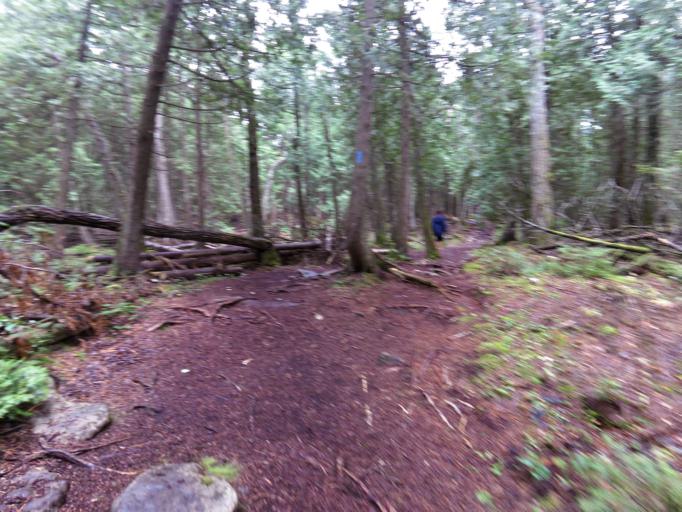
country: CA
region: Ontario
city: Tobermory
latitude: 45.2609
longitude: -81.6493
